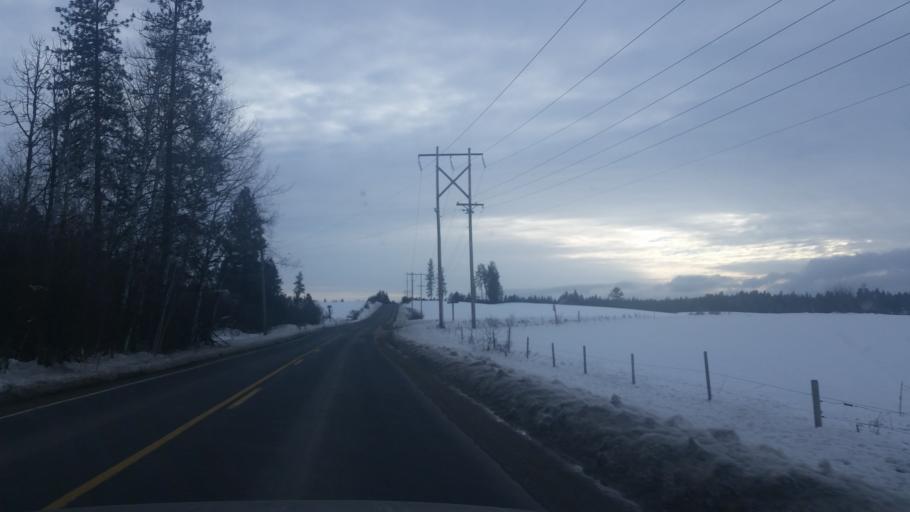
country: US
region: Washington
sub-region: Stevens County
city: Chewelah
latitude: 48.0932
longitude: -117.7580
